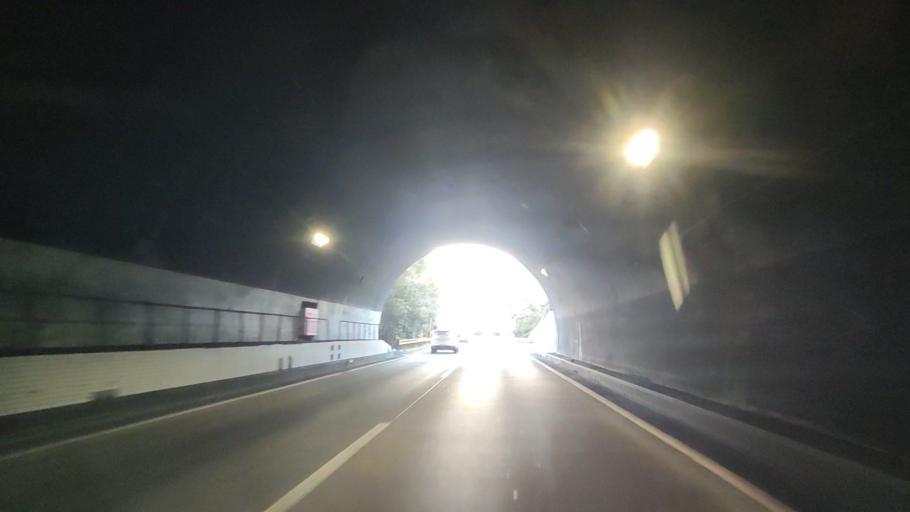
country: JP
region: Okayama
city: Kamogatacho-kamogata
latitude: 34.5591
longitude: 133.6179
